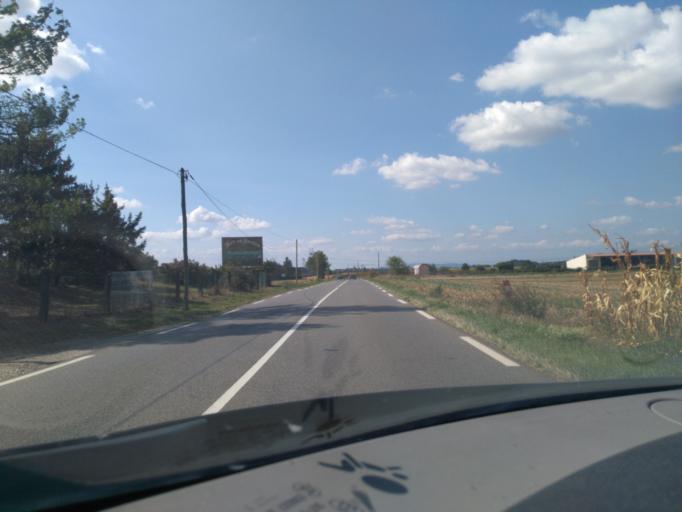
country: FR
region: Rhone-Alpes
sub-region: Departement du Rhone
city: Saint-Bonnet-de-Mure
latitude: 45.7235
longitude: 5.0415
